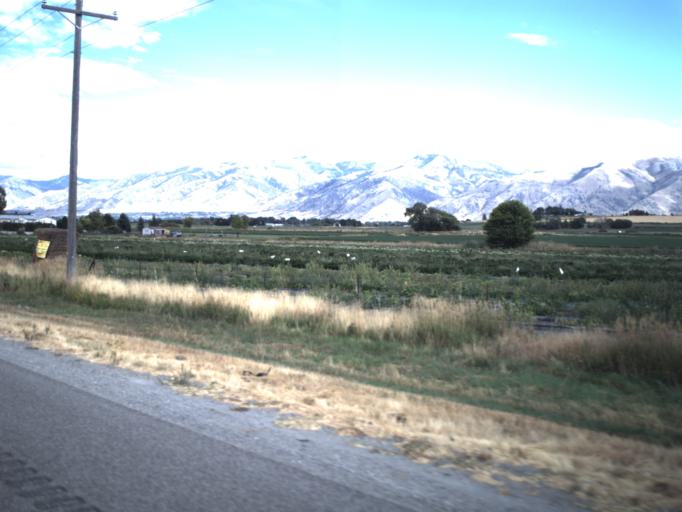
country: US
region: Utah
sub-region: Cache County
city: Wellsville
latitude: 41.6230
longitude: -111.9279
